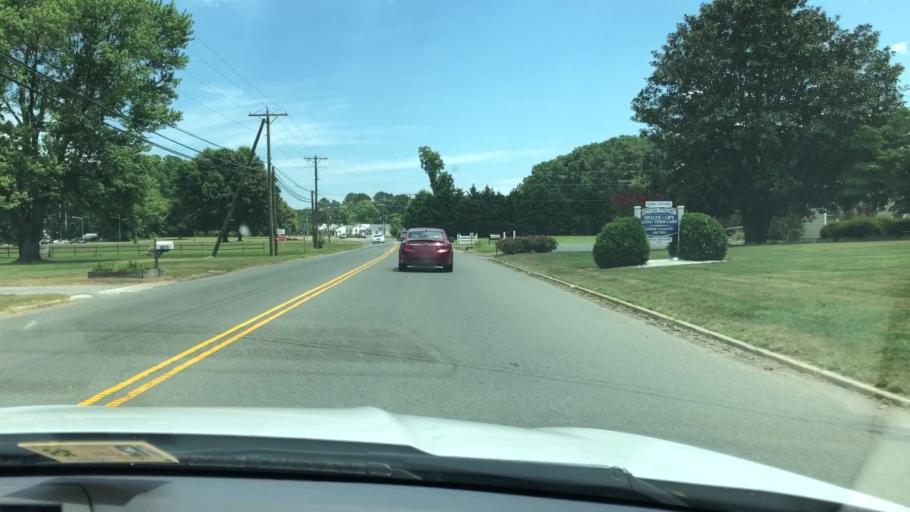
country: US
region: Virginia
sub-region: Lancaster County
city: Lancaster
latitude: 37.7687
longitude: -76.4594
